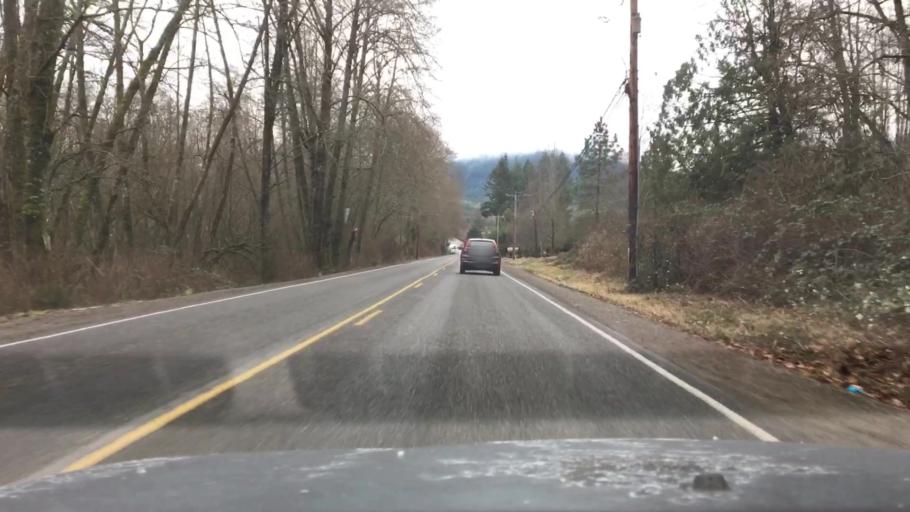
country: US
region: Washington
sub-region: Whatcom County
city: Sudden Valley
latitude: 48.6201
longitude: -122.3340
